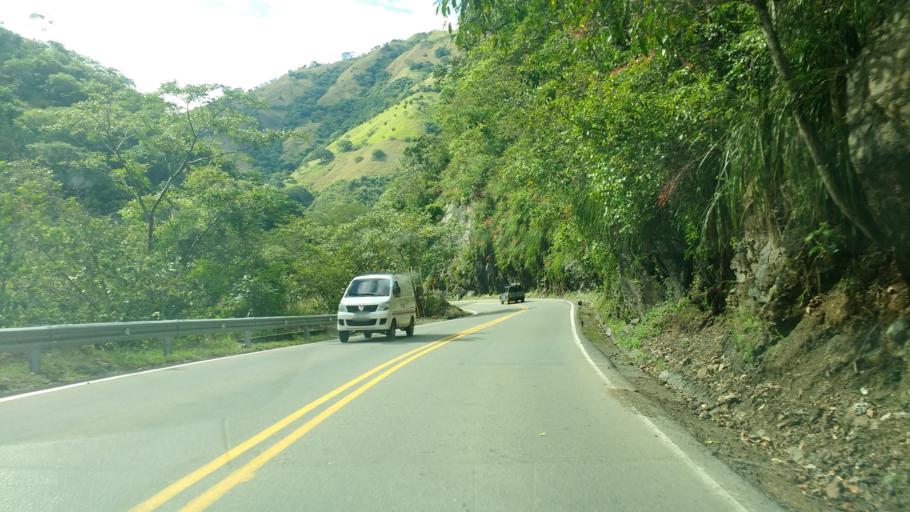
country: CO
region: Antioquia
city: Titiribi
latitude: 6.0023
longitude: -75.7923
